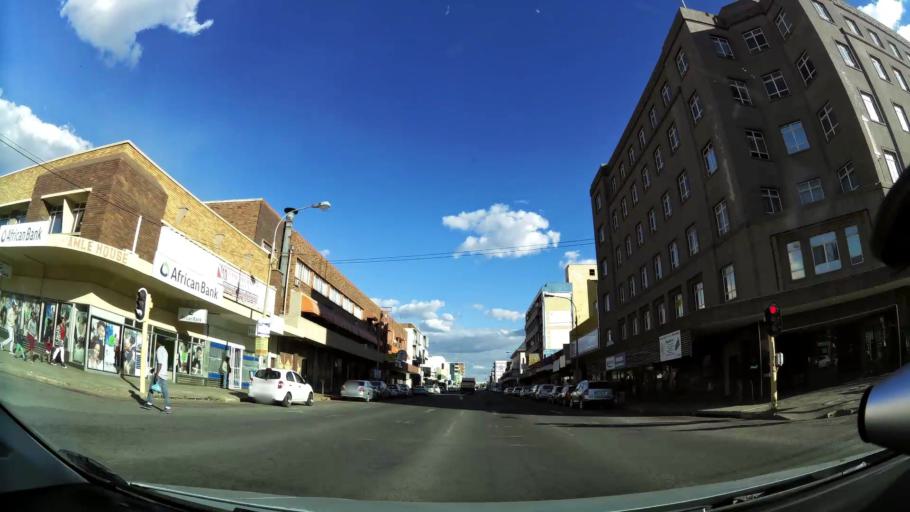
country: ZA
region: North-West
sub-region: Dr Kenneth Kaunda District Municipality
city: Klerksdorp
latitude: -26.8678
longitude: 26.6660
